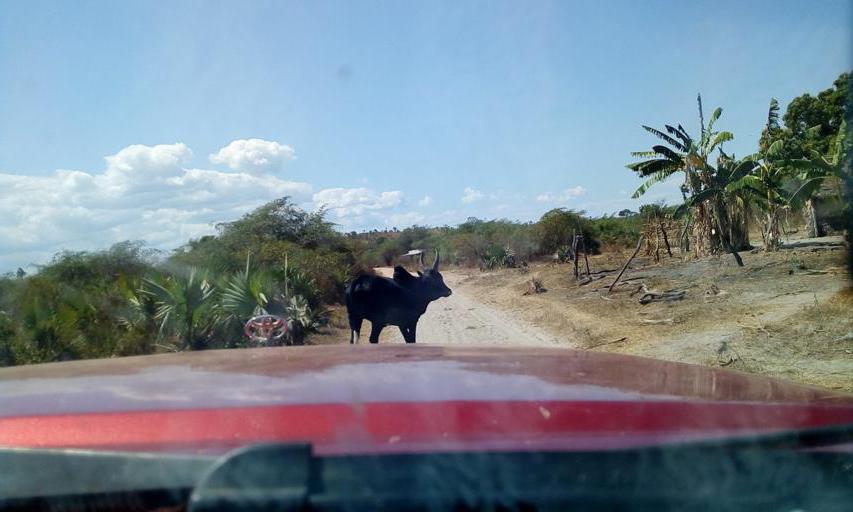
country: MG
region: Boeny
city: Sitampiky
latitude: -16.1236
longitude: 45.5135
